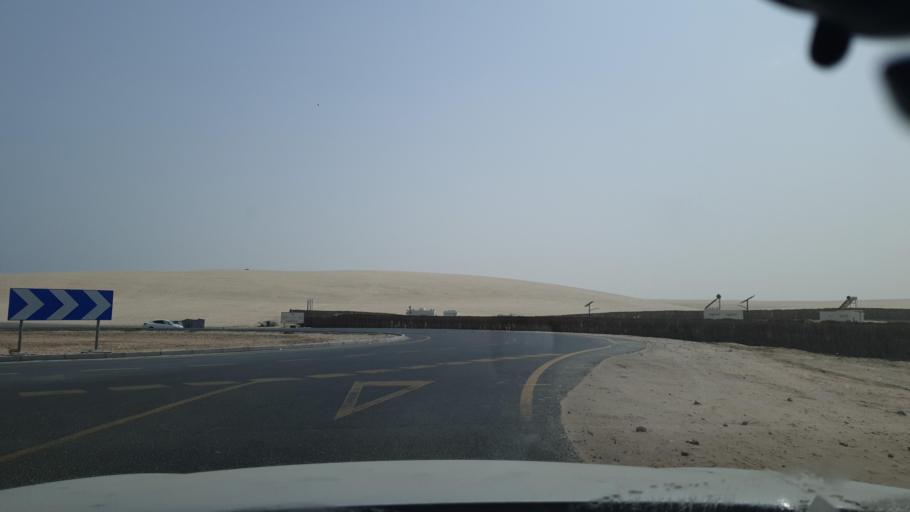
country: QA
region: Al Wakrah
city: Umm Sa'id
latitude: 24.8499
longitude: 51.5078
